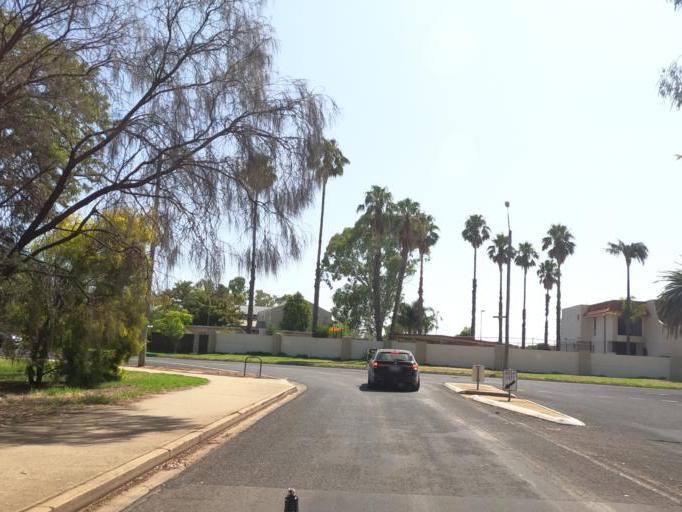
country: AU
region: New South Wales
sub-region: Corowa Shire
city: Mulwala
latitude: -36.0010
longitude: 146.0010
